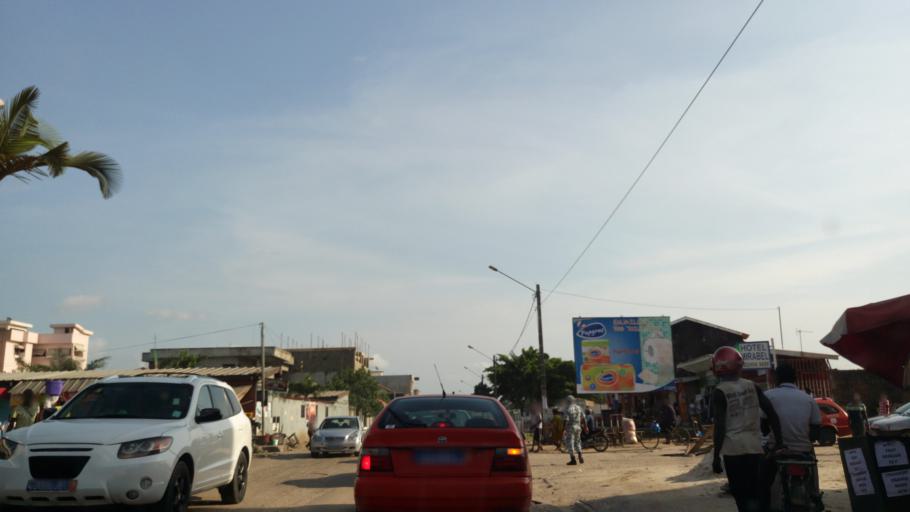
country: CI
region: Lagunes
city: Abobo
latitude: 5.3692
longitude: -3.9590
